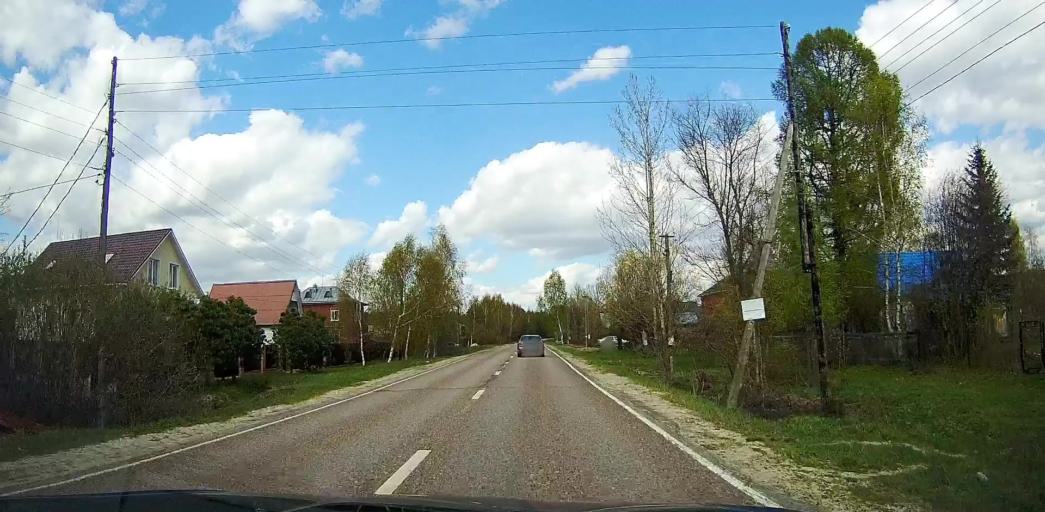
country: RU
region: Moskovskaya
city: Davydovo
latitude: 55.5879
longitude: 38.8301
